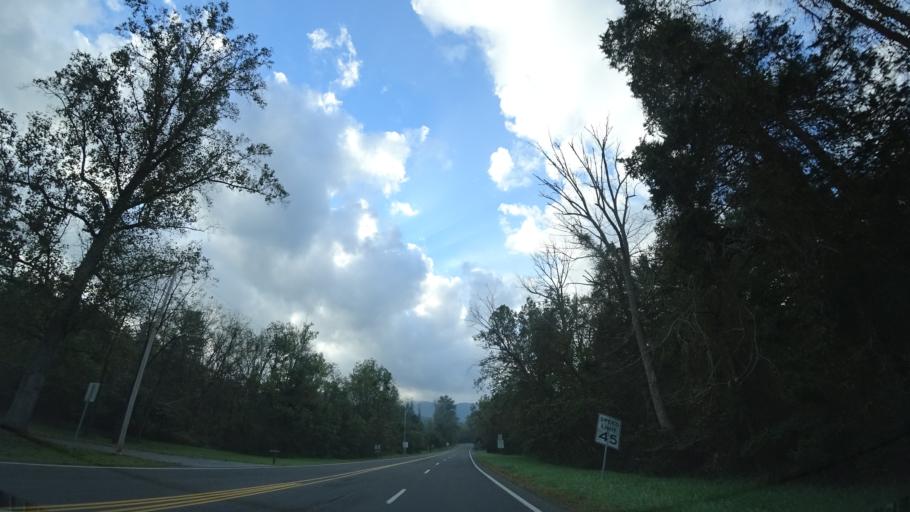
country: US
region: Virginia
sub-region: Page County
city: Luray
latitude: 38.6626
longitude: -78.3726
